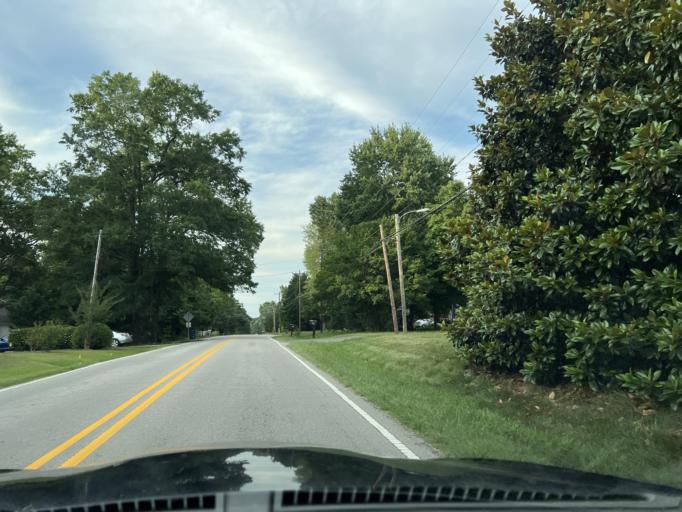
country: US
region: North Carolina
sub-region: Durham County
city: Durham
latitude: 35.9745
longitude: -78.8434
